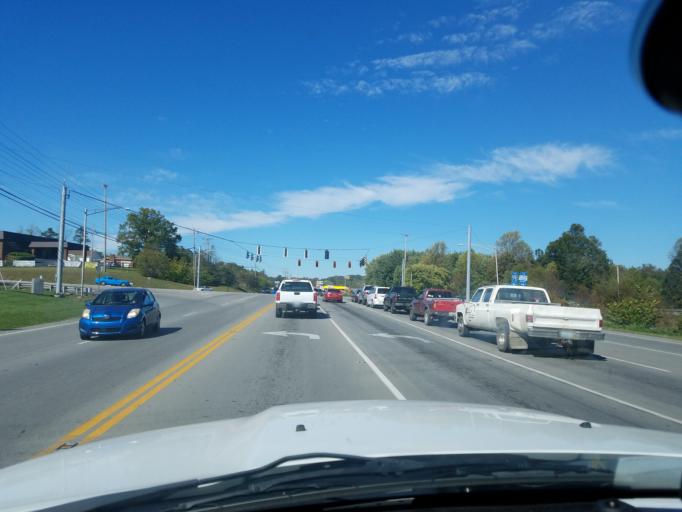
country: US
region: Kentucky
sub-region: Laurel County
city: London
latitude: 37.1068
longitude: -84.0721
